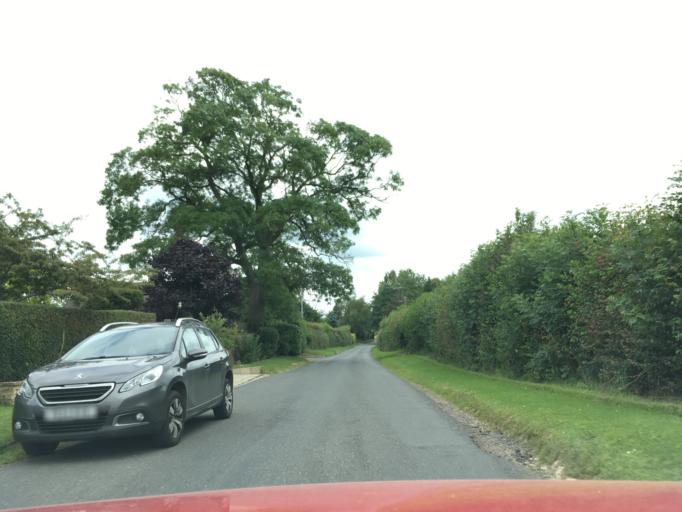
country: GB
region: England
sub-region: Oxfordshire
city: Shipton under Wychwood
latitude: 51.8933
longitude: -1.6413
